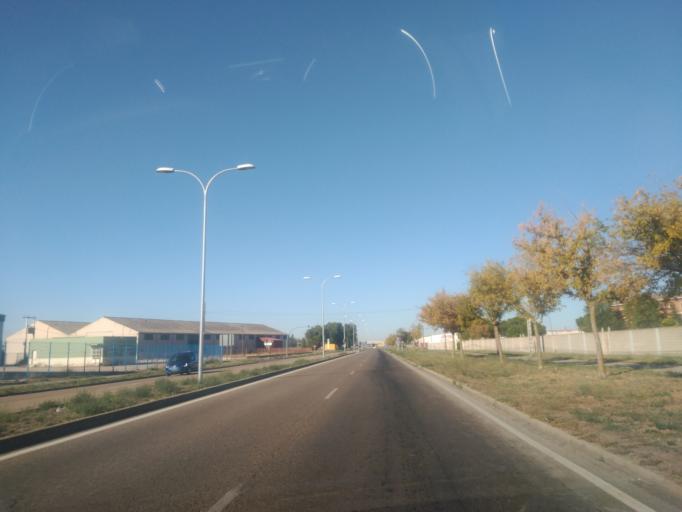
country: ES
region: Castille and Leon
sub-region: Provincia de Burgos
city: Villalba de Duero
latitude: 41.6656
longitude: -3.7195
